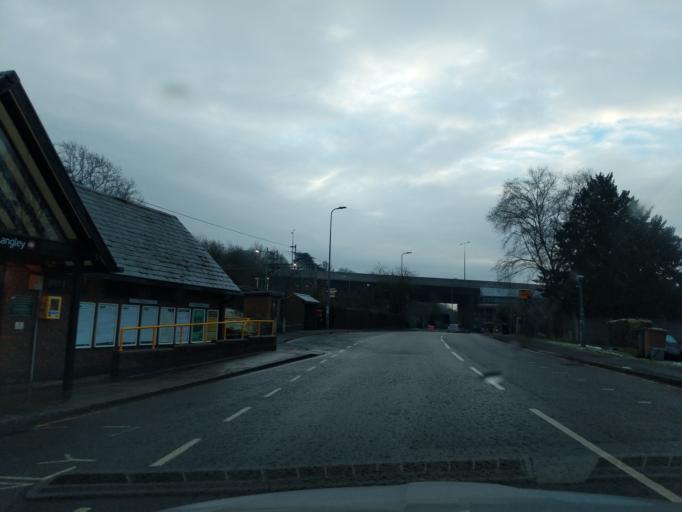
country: GB
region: England
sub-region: Hertfordshire
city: Kings Langley
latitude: 51.7064
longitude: -0.4385
